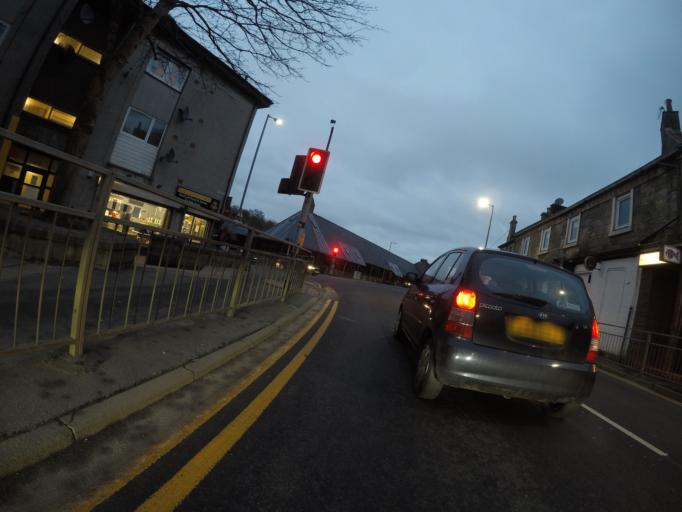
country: GB
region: Scotland
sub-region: North Ayrshire
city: Kilwinning
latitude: 55.6538
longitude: -4.7050
